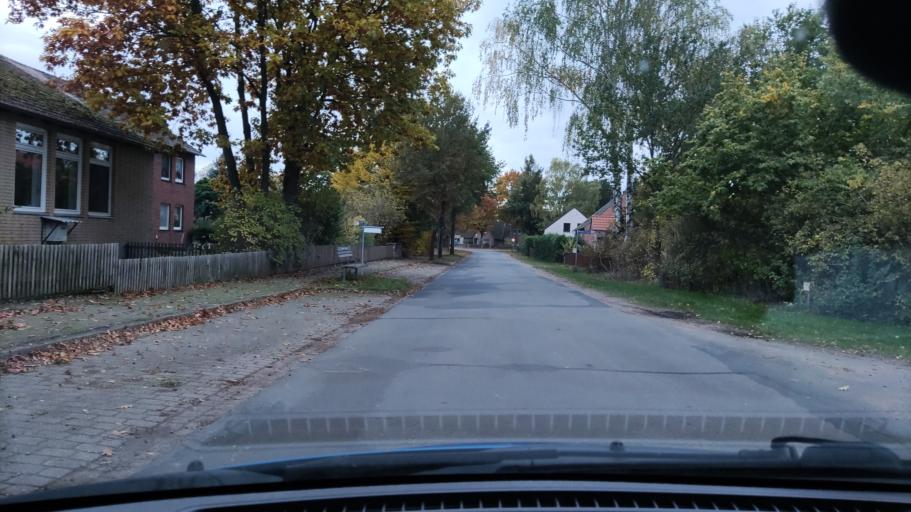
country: DE
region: Lower Saxony
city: Prezelle
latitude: 52.9655
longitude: 11.3999
